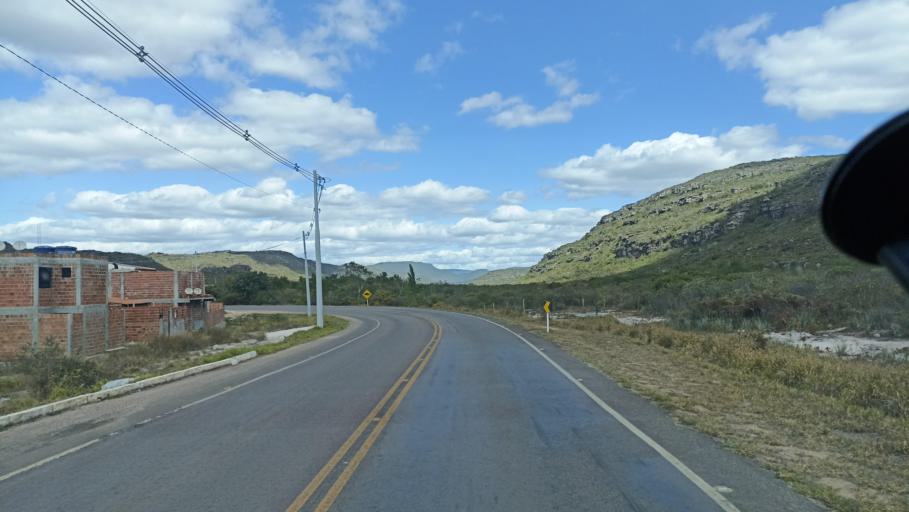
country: BR
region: Bahia
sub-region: Andarai
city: Vera Cruz
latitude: -13.0129
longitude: -41.3732
